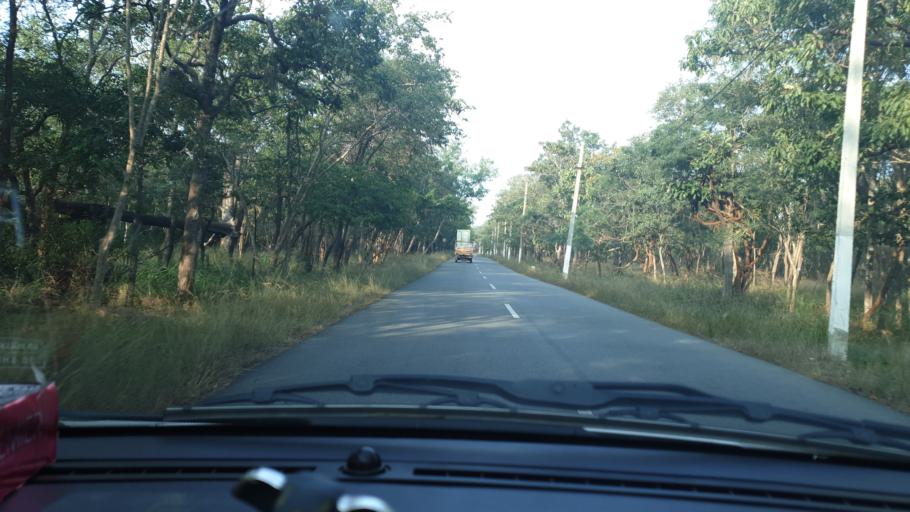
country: IN
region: Andhra Pradesh
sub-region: Kurnool
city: Srisailam
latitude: 16.2866
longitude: 78.7282
